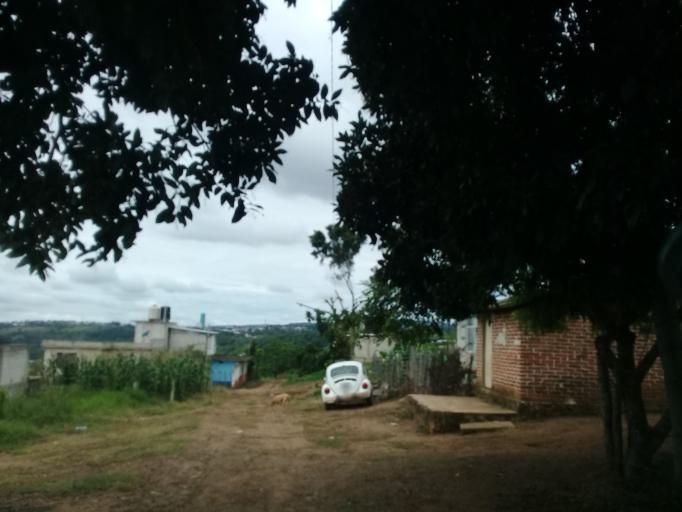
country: MX
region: Veracruz
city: El Castillo
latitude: 19.5546
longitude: -96.8798
